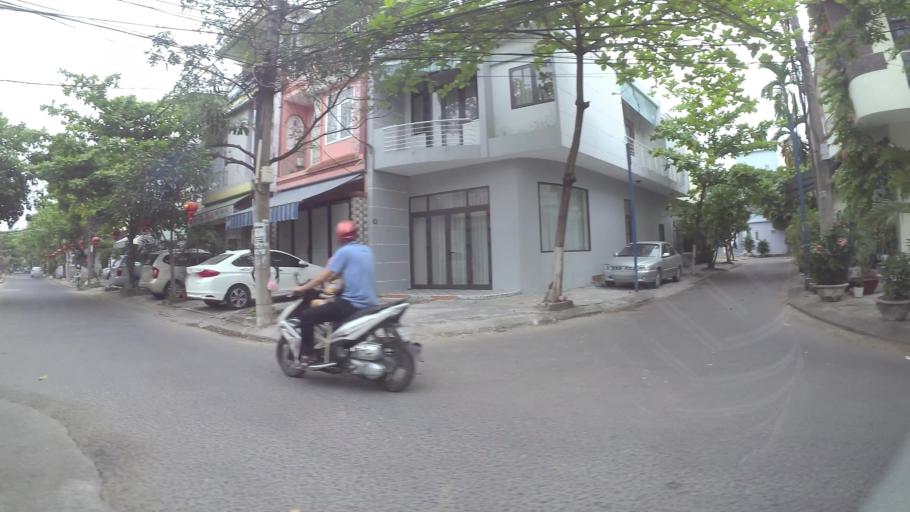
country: VN
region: Da Nang
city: Thanh Khe
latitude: 16.0576
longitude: 108.1883
